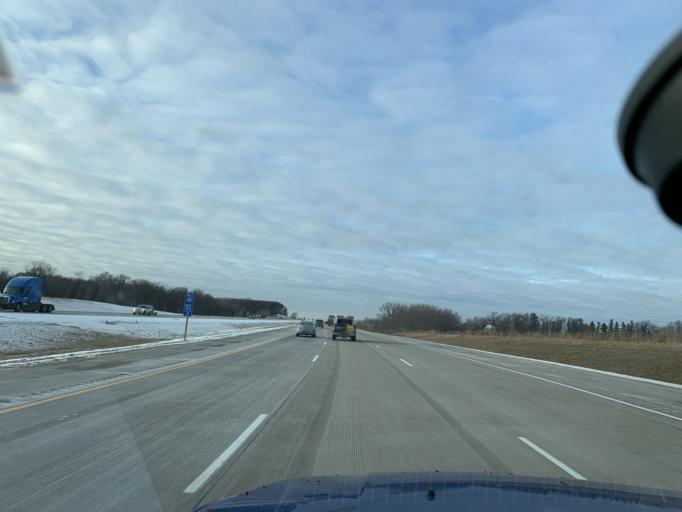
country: US
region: Wisconsin
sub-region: Dane County
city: Deerfield
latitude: 42.9634
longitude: -89.1008
